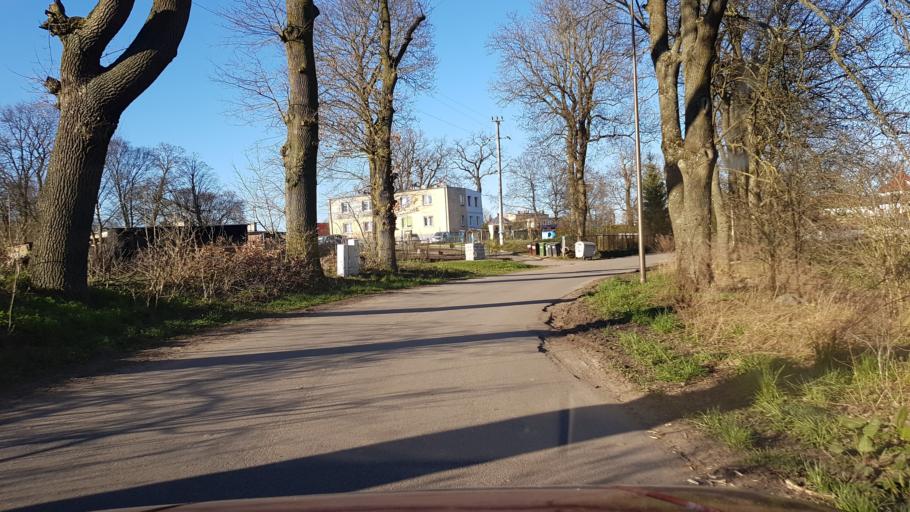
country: PL
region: West Pomeranian Voivodeship
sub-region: Powiat stargardzki
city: Stara Dabrowa
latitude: 53.3755
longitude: 15.1071
